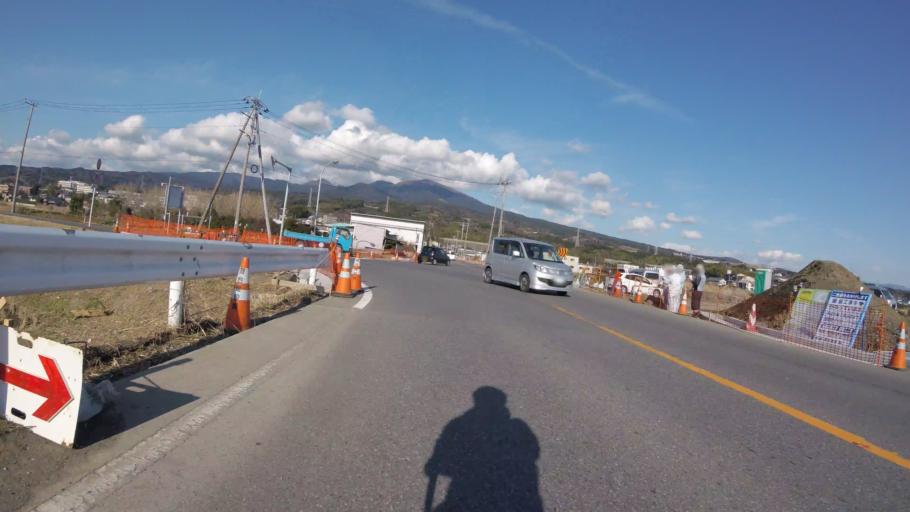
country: JP
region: Shizuoka
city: Numazu
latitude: 35.1423
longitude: 138.7858
